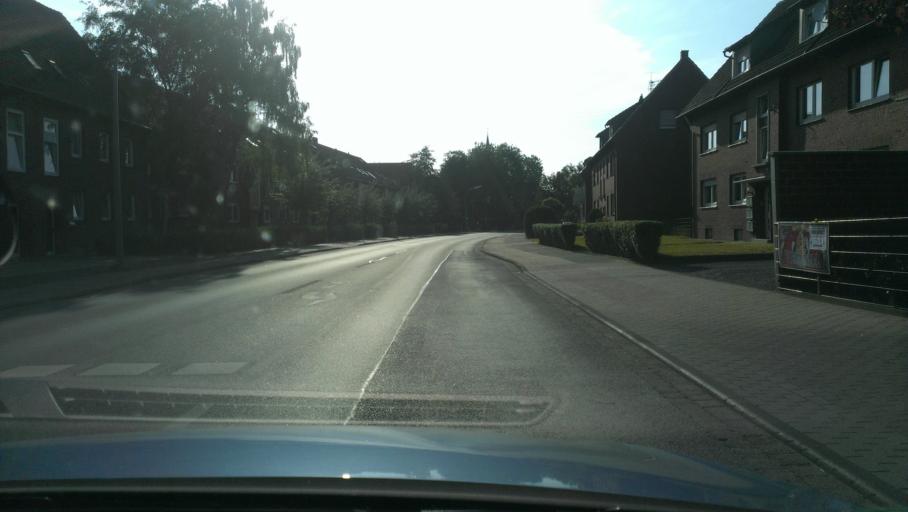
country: DE
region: North Rhine-Westphalia
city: Sendenhorst
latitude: 51.8426
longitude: 7.8343
